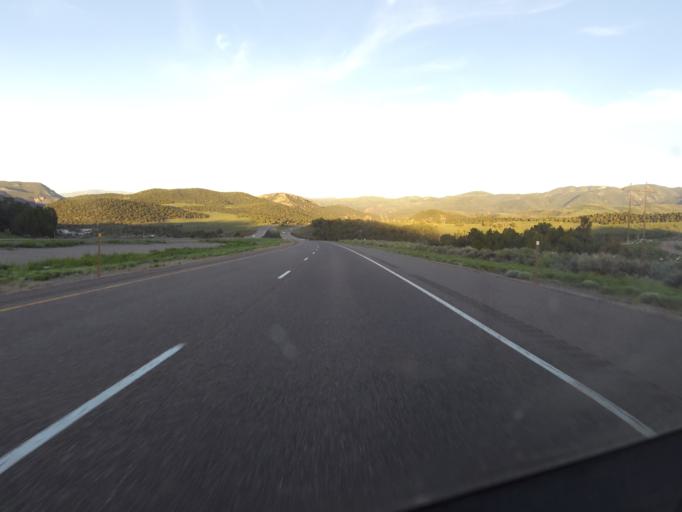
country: US
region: Utah
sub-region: Beaver County
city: Beaver
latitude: 38.5745
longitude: -112.4671
